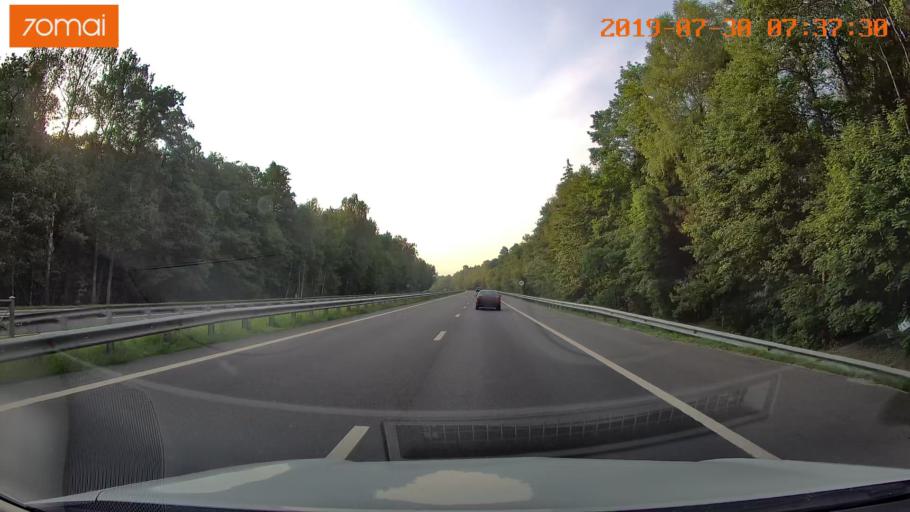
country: RU
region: Kaliningrad
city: Gvardeysk
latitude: 54.6554
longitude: 21.1472
